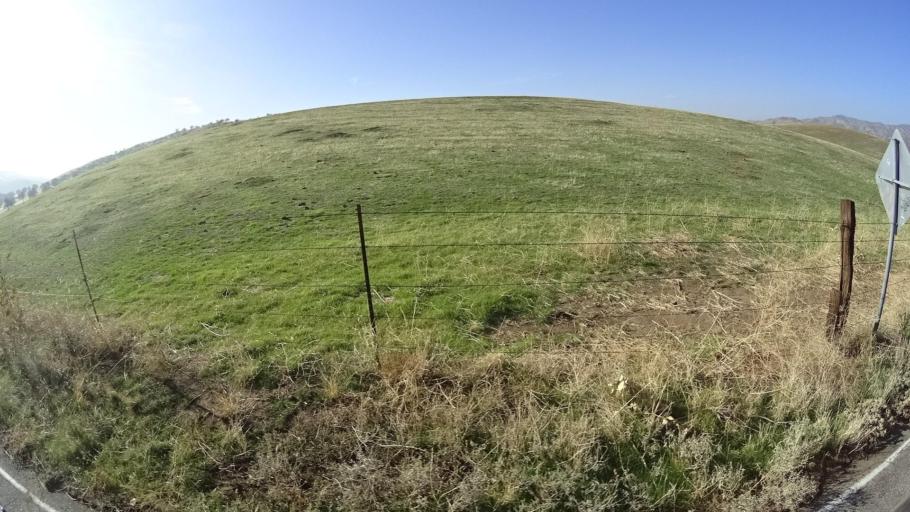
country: US
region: California
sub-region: Kern County
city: Bear Valley Springs
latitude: 35.2745
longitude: -118.6244
